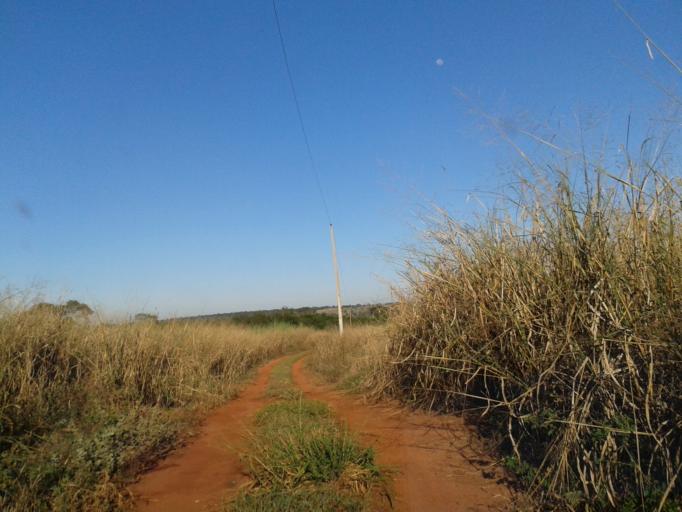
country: BR
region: Minas Gerais
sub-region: Santa Vitoria
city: Santa Vitoria
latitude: -19.0226
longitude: -50.3648
